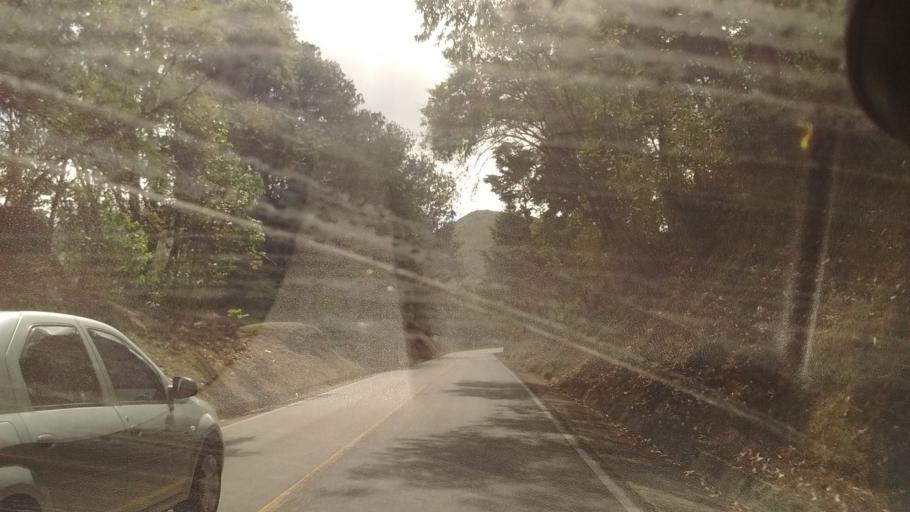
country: CO
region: Cauca
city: Cajibio
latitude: 2.6217
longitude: -76.5073
